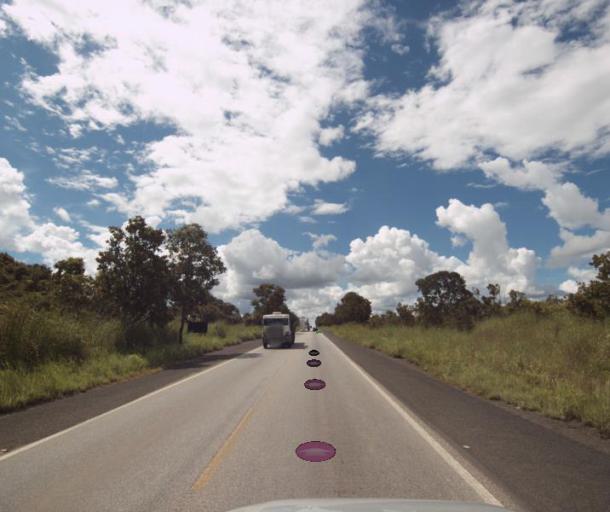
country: BR
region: Goias
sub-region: Porangatu
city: Porangatu
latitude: -13.8478
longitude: -49.0474
